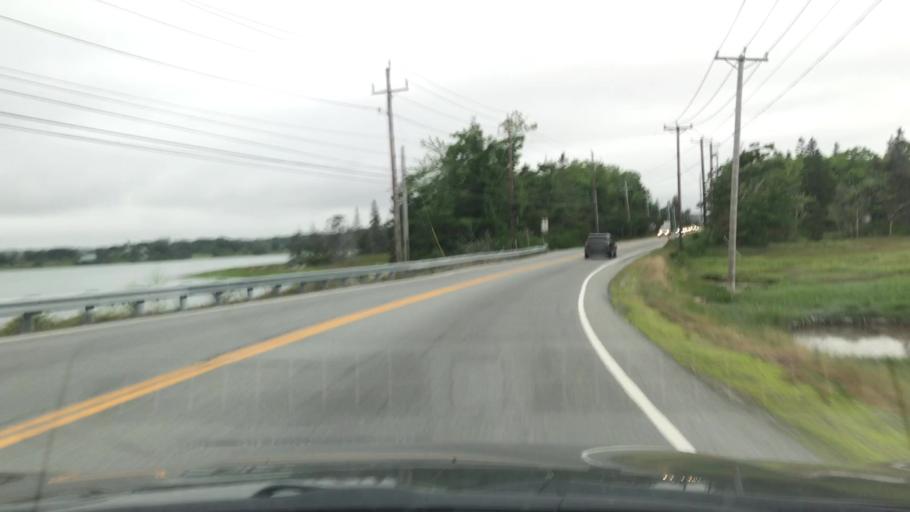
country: US
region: Maine
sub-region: Hancock County
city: Trenton
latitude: 44.4220
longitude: -68.3640
